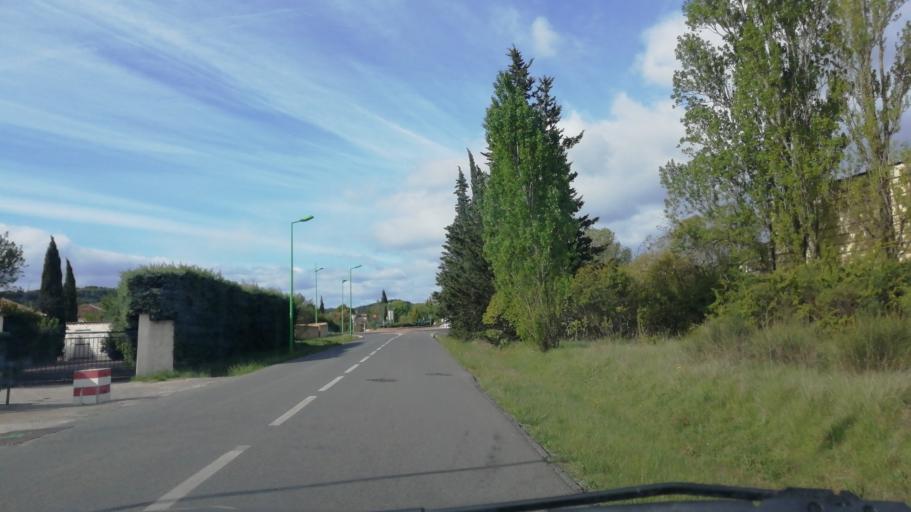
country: FR
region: Languedoc-Roussillon
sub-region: Departement de l'Herault
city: Saint-Martin-de-Londres
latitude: 43.7837
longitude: 3.7276
